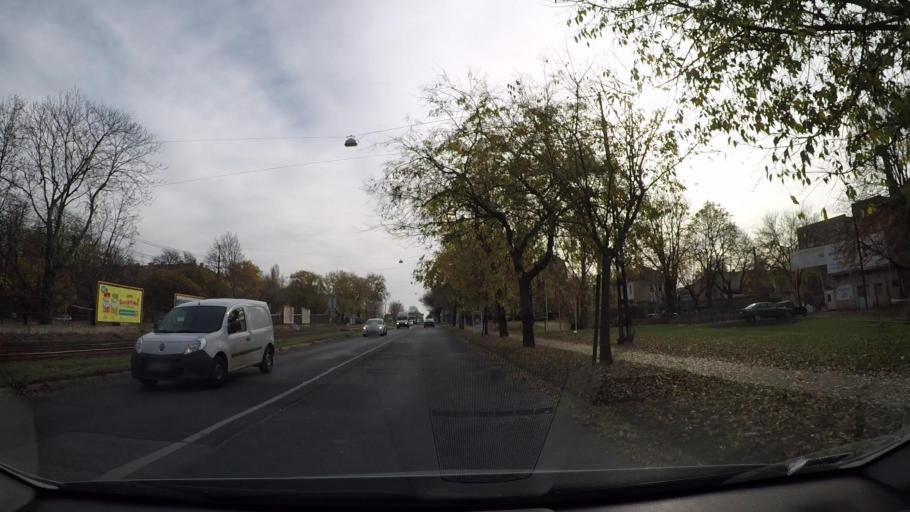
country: HU
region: Budapest
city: Budapest X. keruelet
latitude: 47.4858
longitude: 19.1545
